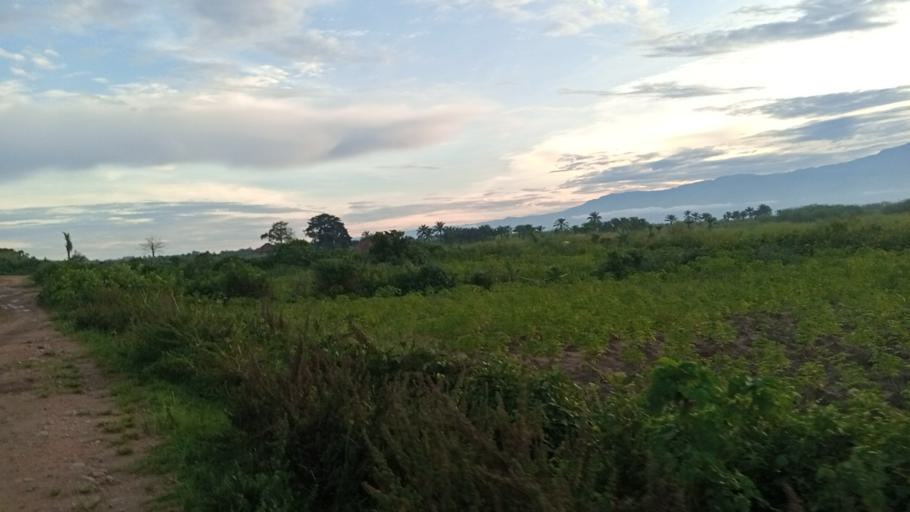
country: BI
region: Bujumbura Mairie
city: Bujumbura
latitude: -3.4692
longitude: 29.3418
